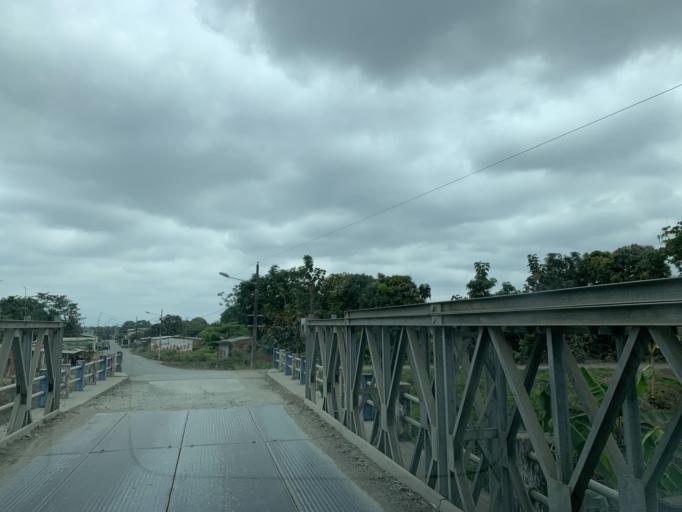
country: EC
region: Guayas
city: Coronel Marcelino Mariduena
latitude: -2.3193
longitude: -79.4707
